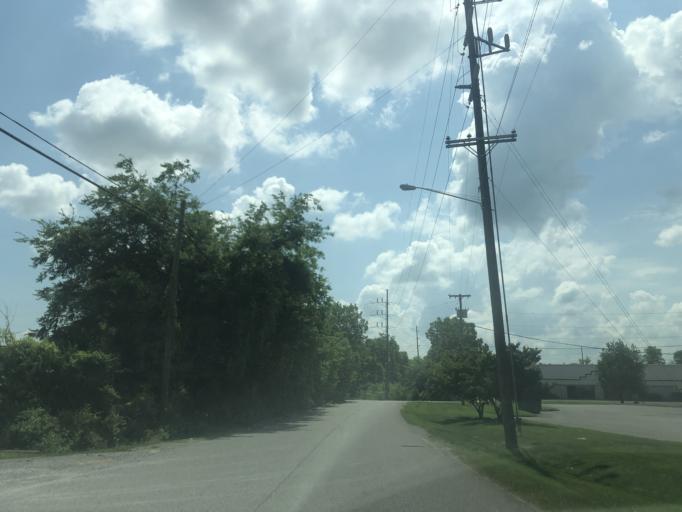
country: US
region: Tennessee
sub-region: Rutherford County
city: La Vergne
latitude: 36.0161
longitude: -86.6015
